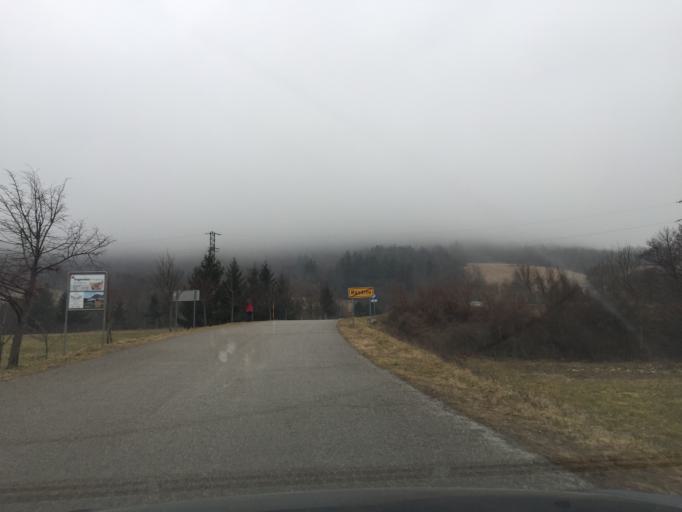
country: SI
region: Divaca
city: Divaca
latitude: 45.7584
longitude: 14.0620
